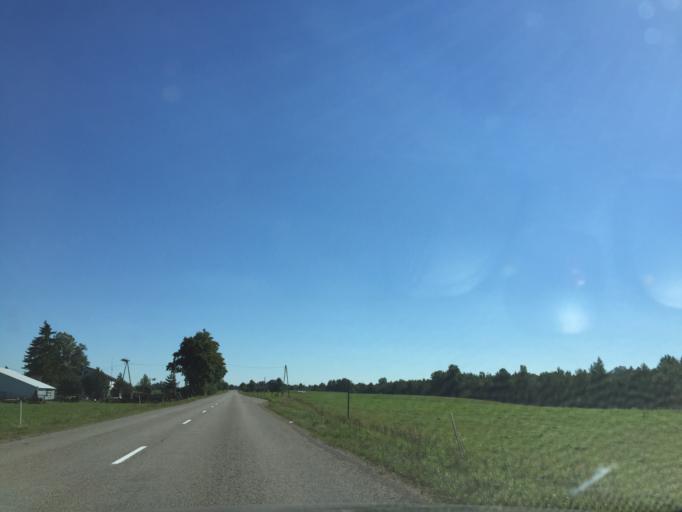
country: LV
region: Akniste
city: Akniste
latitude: 56.0661
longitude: 25.8936
